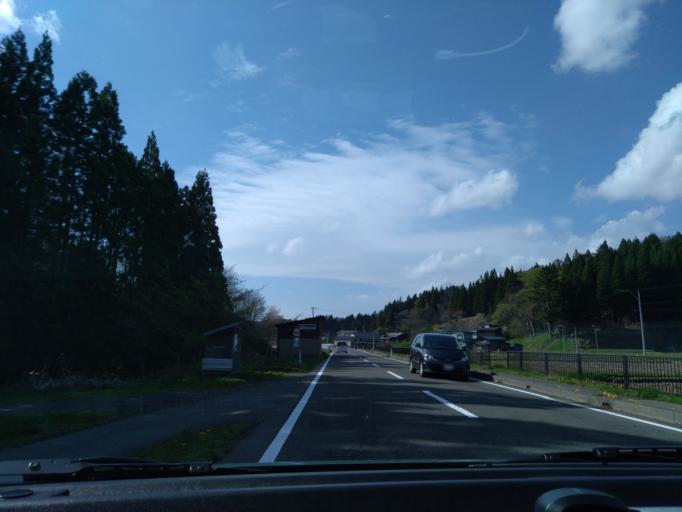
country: JP
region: Akita
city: Akita
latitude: 39.7104
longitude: 140.2043
